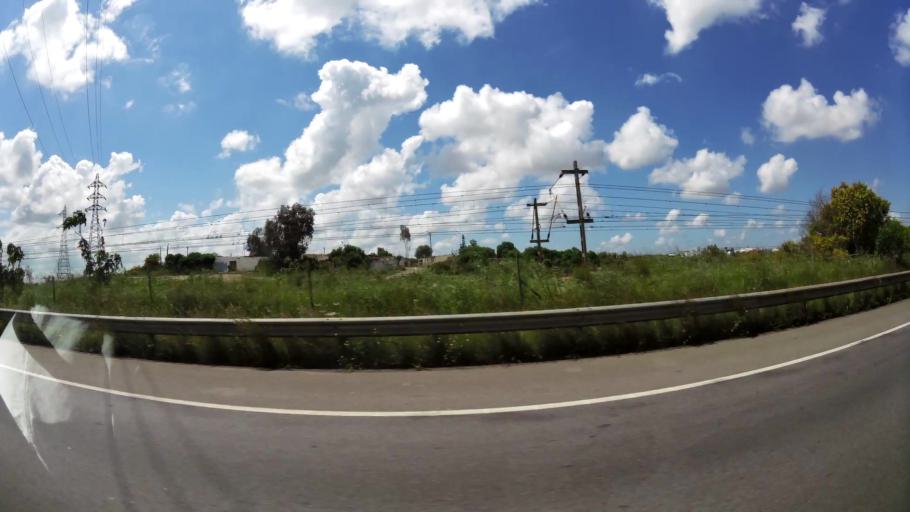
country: MA
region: Grand Casablanca
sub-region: Nouaceur
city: Bouskoura
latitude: 33.4208
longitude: -7.6274
